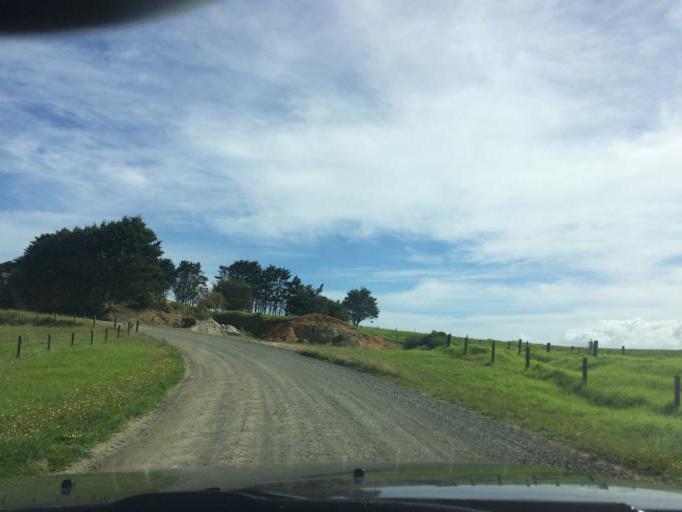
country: NZ
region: Northland
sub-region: Kaipara District
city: Dargaville
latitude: -35.9579
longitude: 173.7692
